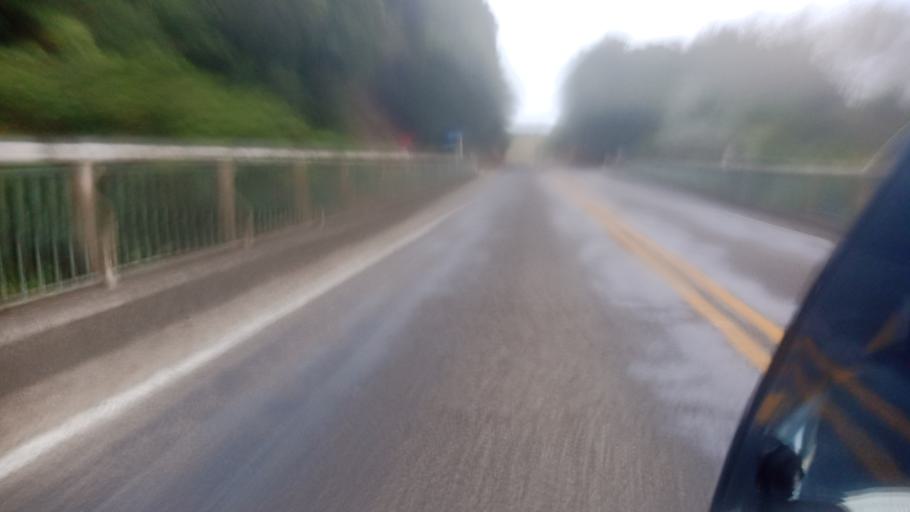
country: NZ
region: Bay of Plenty
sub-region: Opotiki District
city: Opotiki
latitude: -38.4153
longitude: 177.5606
